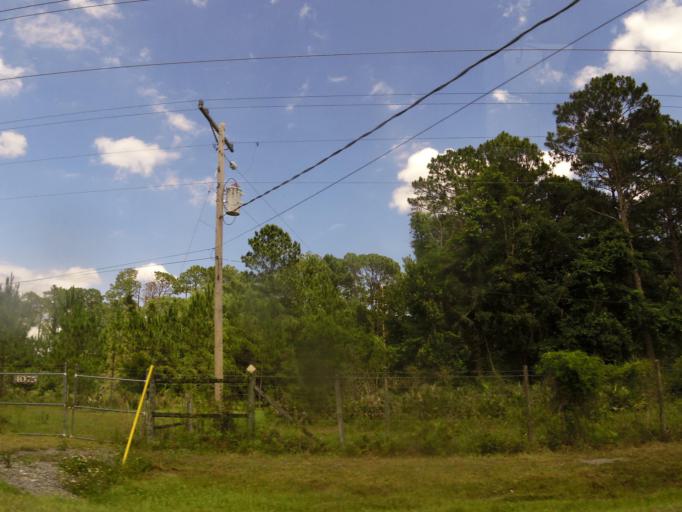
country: US
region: Florida
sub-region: Clay County
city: Green Cove Springs
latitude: 29.9773
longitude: -81.7394
